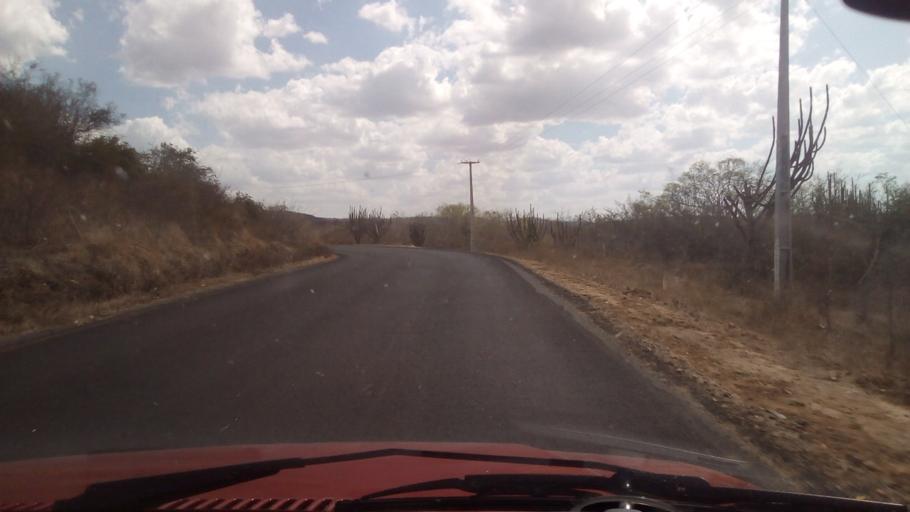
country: BR
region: Paraiba
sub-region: Cacimba De Dentro
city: Cacimba de Dentro
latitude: -6.6847
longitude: -35.7445
